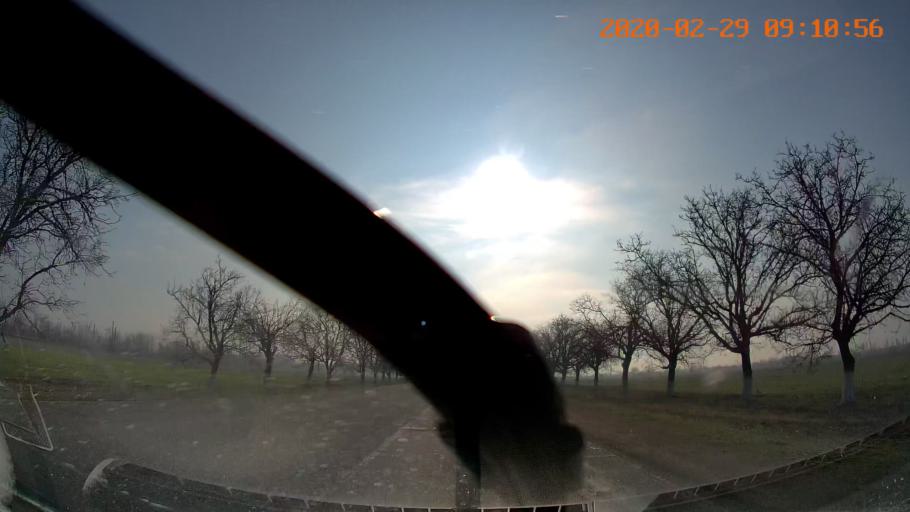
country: MD
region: Telenesti
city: Slobozia
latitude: 46.8396
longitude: 29.7910
